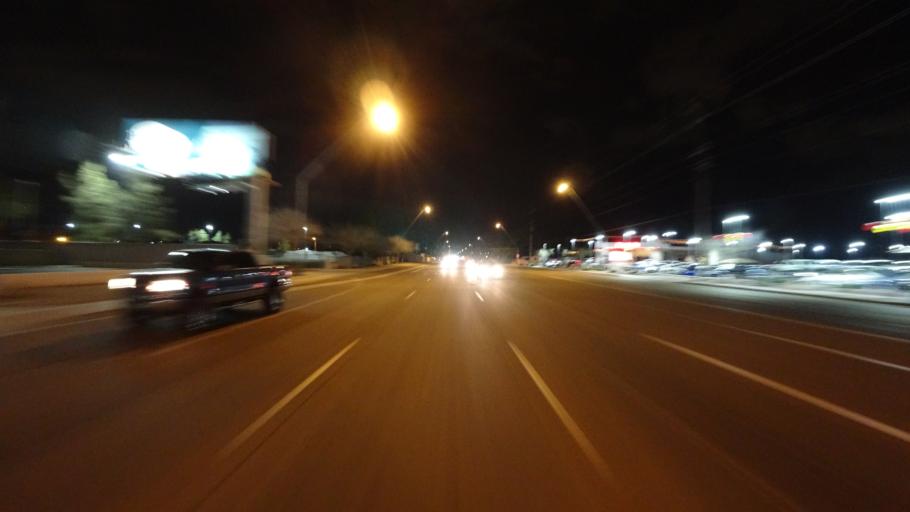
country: US
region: Arizona
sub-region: Maricopa County
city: Mesa
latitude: 33.4070
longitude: -111.8567
